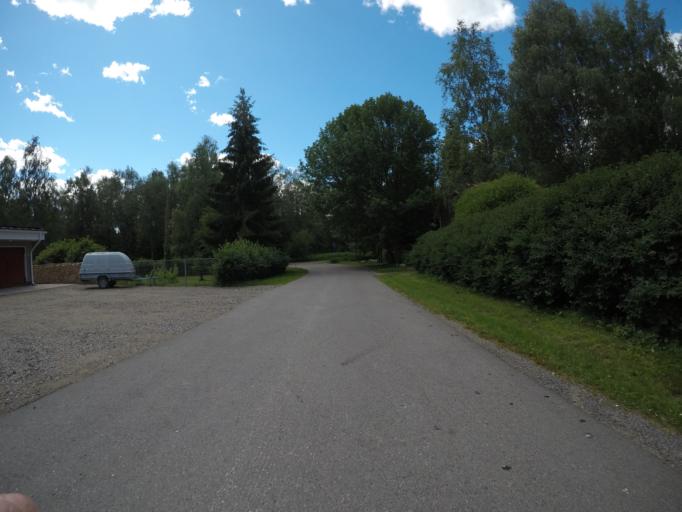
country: FI
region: Haeme
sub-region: Haemeenlinna
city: Haemeenlinna
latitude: 61.0102
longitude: 24.4296
